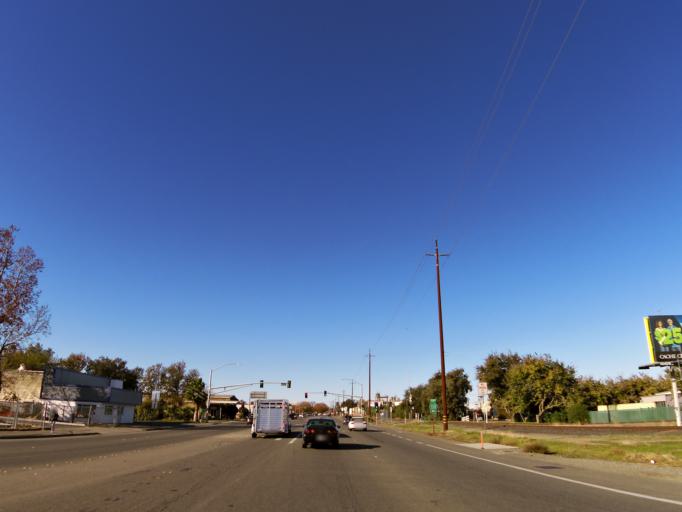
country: US
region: California
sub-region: Yolo County
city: Woodland
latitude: 38.6773
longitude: -121.7517
